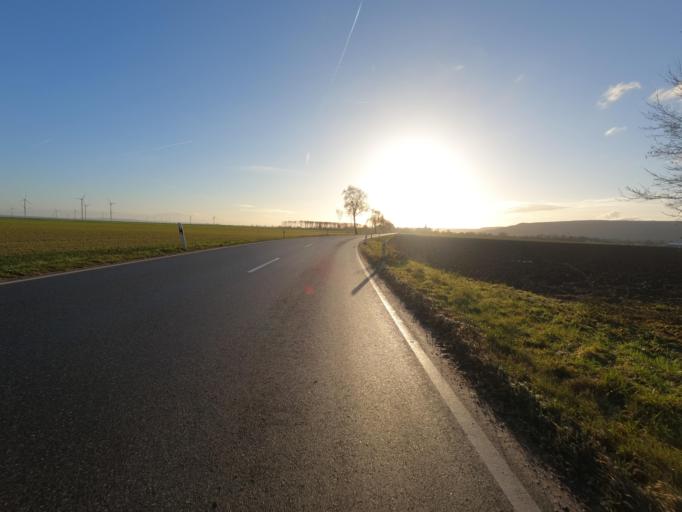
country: DE
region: North Rhine-Westphalia
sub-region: Regierungsbezirk Koln
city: Titz
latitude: 50.9743
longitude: 6.4500
